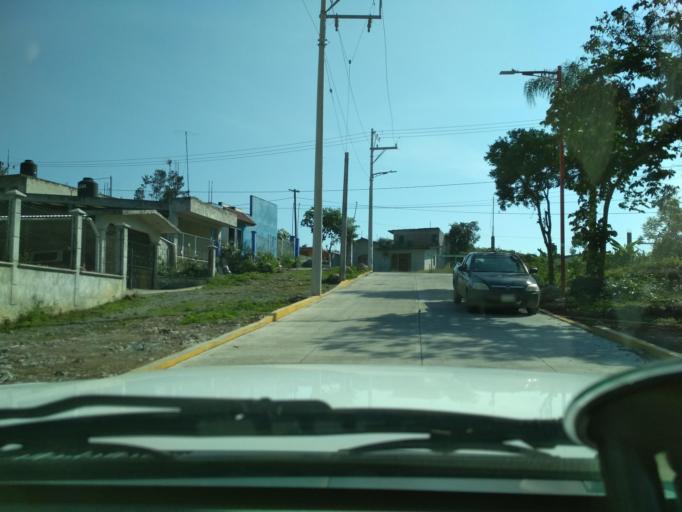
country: MX
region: Veracruz
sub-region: Chocaman
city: San Jose Neria
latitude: 19.0010
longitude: -97.0037
